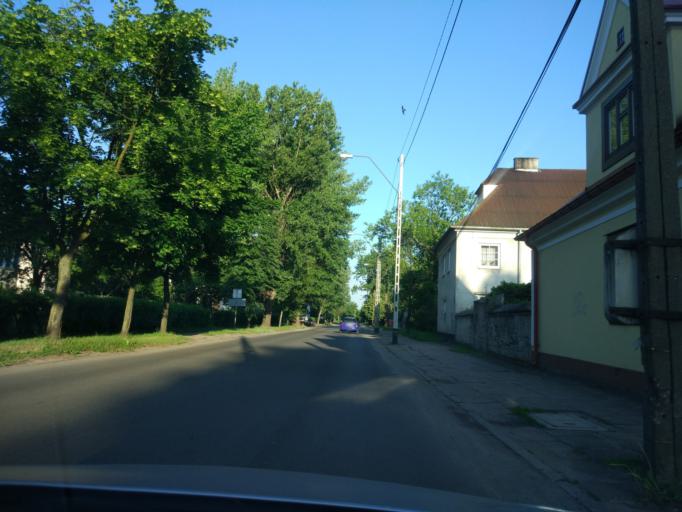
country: PL
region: Lodz Voivodeship
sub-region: Powiat kutnowski
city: Kutno
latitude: 52.2266
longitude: 19.3524
